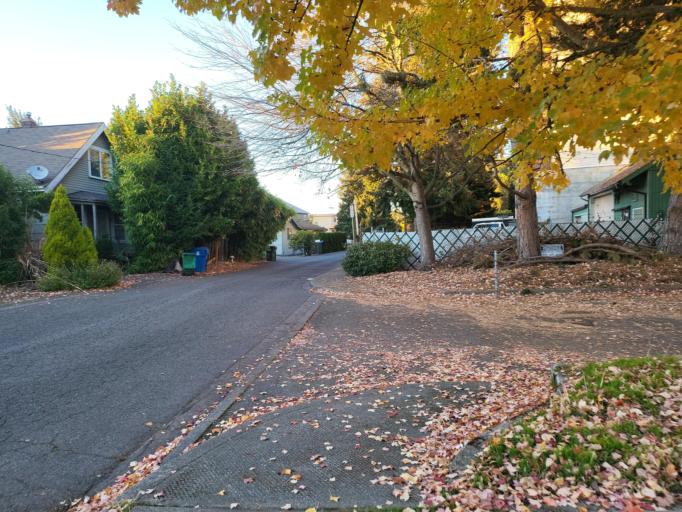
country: US
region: Washington
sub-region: King County
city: Renton
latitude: 47.4823
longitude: -122.2084
